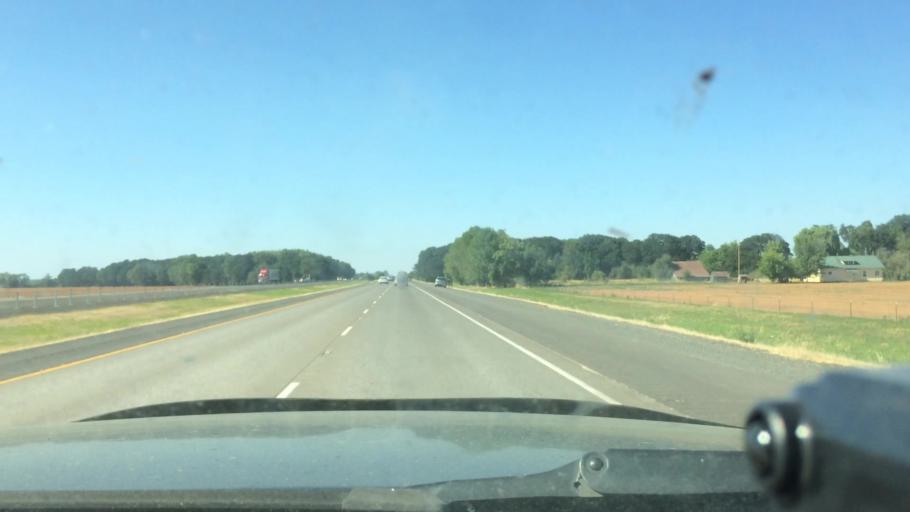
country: US
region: Oregon
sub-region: Linn County
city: Tangent
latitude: 44.4683
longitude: -123.0605
